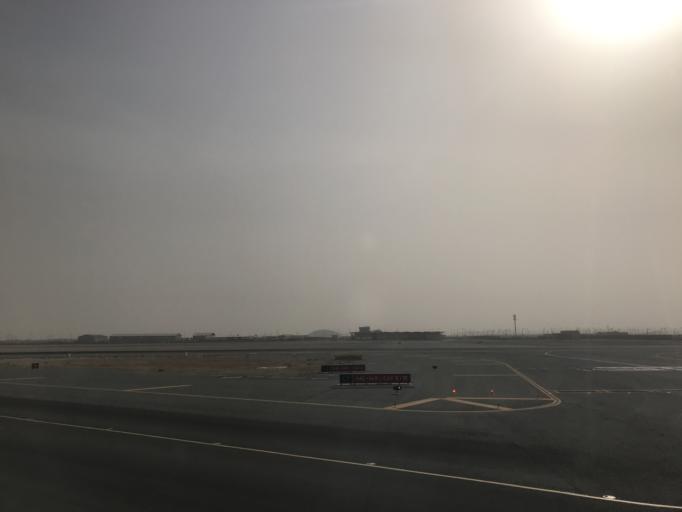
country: QA
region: Baladiyat ad Dawhah
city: Doha
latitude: 25.2753
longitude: 51.5987
